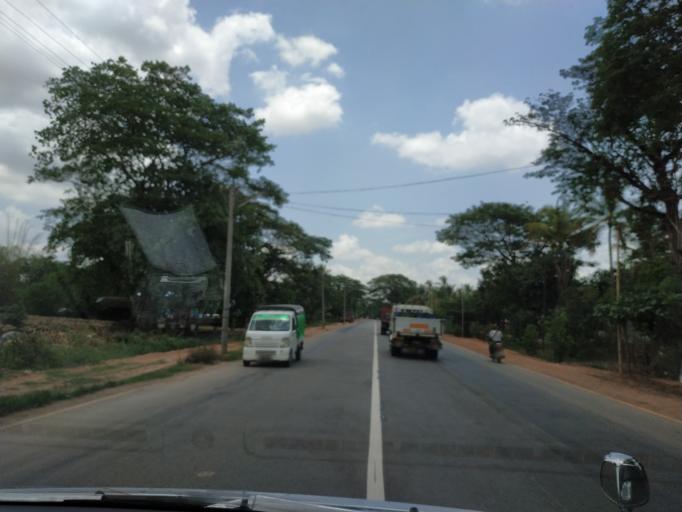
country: MM
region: Bago
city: Bago
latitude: 17.4671
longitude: 96.5815
